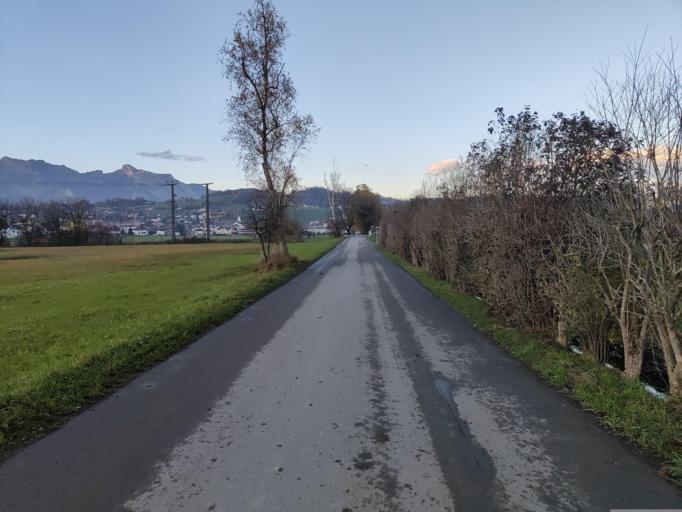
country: LI
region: Eschen
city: Eschen
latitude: 47.2022
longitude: 9.5260
